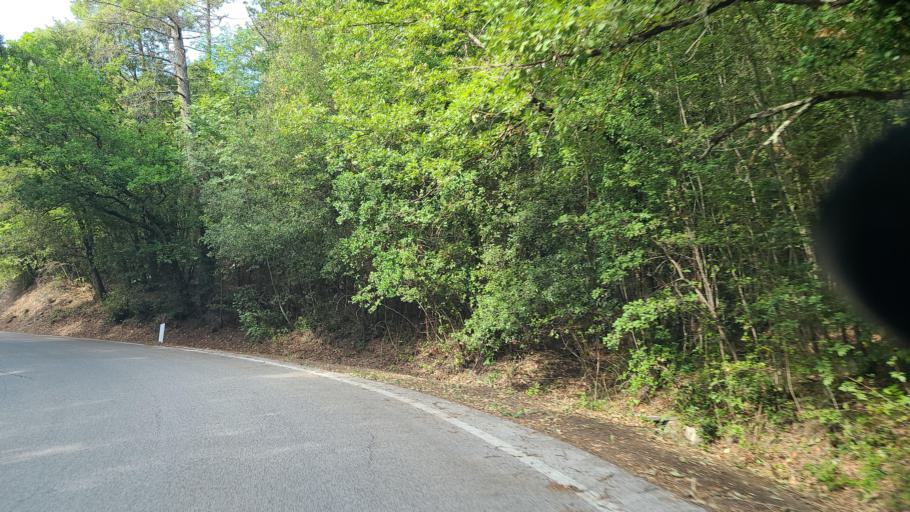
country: IT
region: Tuscany
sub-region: Provincia di Siena
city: San Gimignano
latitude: 43.4171
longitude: 10.9764
